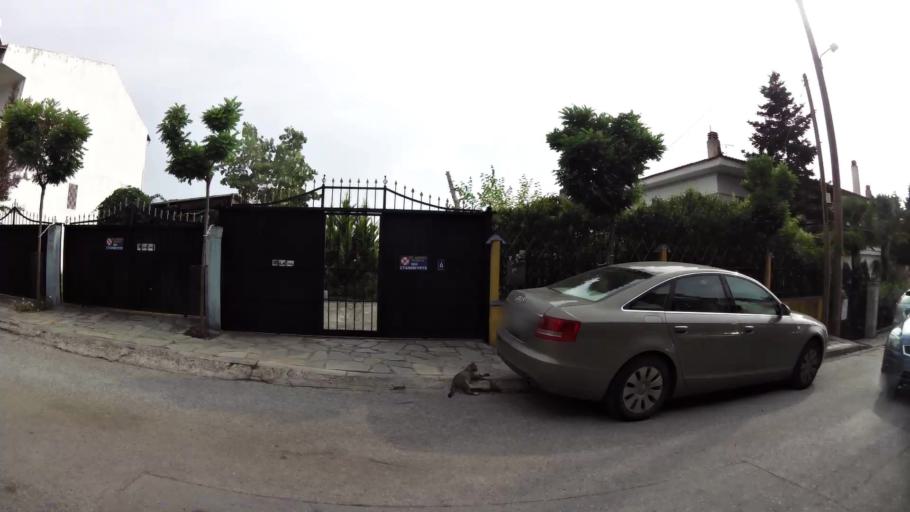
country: GR
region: Central Macedonia
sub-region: Nomos Thessalonikis
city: Oraiokastro
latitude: 40.7342
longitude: 22.9171
